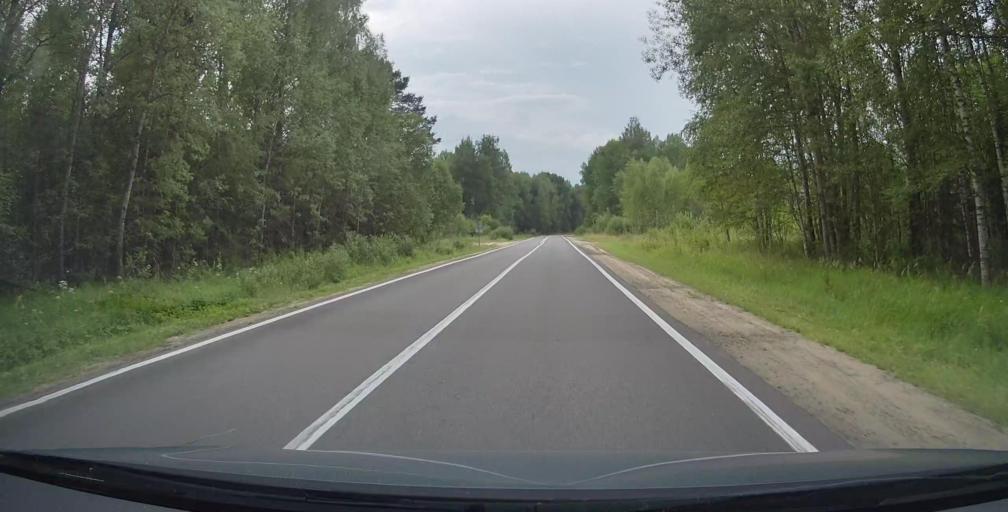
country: RU
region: Jaroslavl
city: Rybinsk
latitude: 57.9369
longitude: 38.6769
